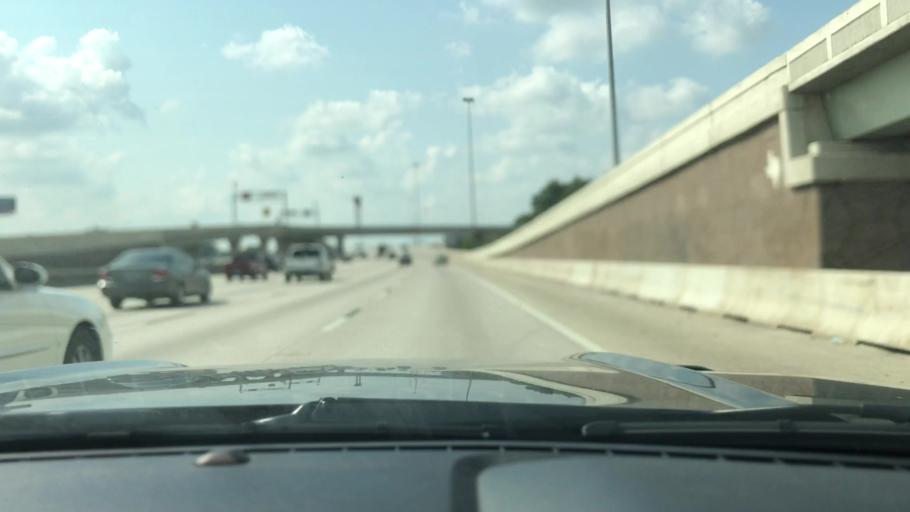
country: US
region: Texas
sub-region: Harris County
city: Aldine
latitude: 29.8535
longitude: -95.3340
